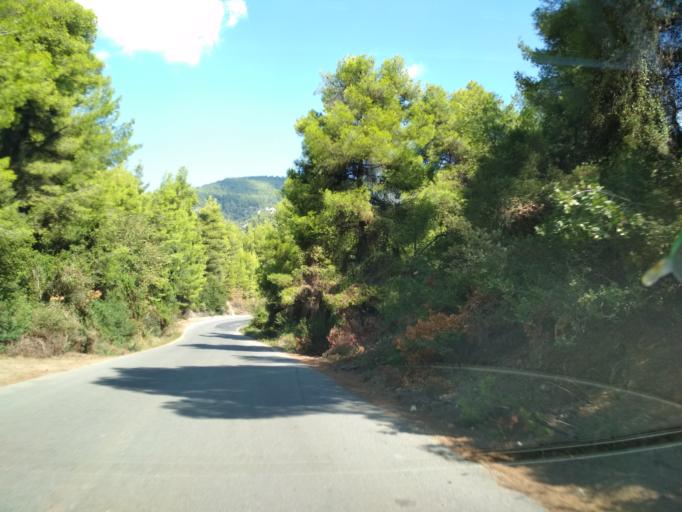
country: GR
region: Central Greece
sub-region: Nomos Evvoias
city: Roviai
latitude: 38.8231
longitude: 23.2507
